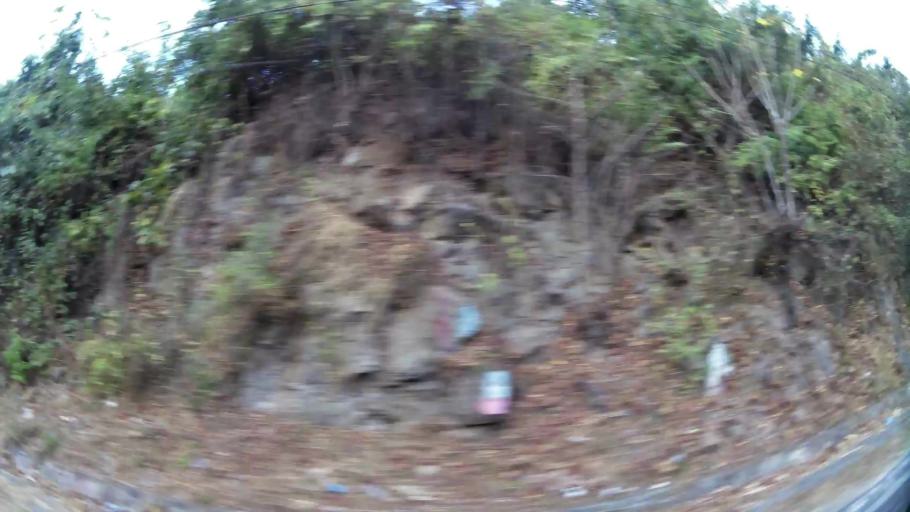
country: SV
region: San Vicente
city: Apastepeque
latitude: 13.6629
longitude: -88.7937
